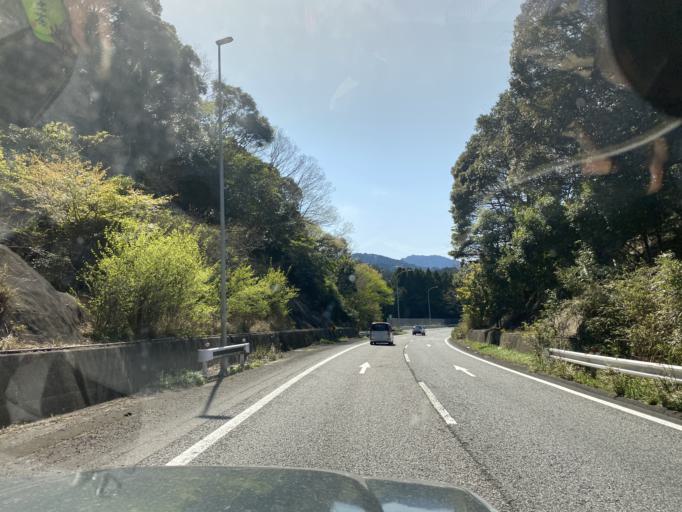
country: JP
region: Mie
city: Kameyama
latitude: 34.8363
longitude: 136.3390
